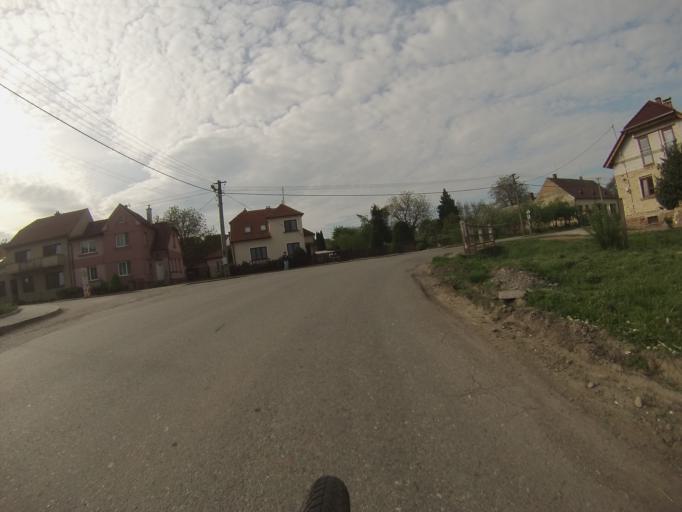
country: CZ
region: South Moravian
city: Cebin
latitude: 49.3139
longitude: 16.4523
